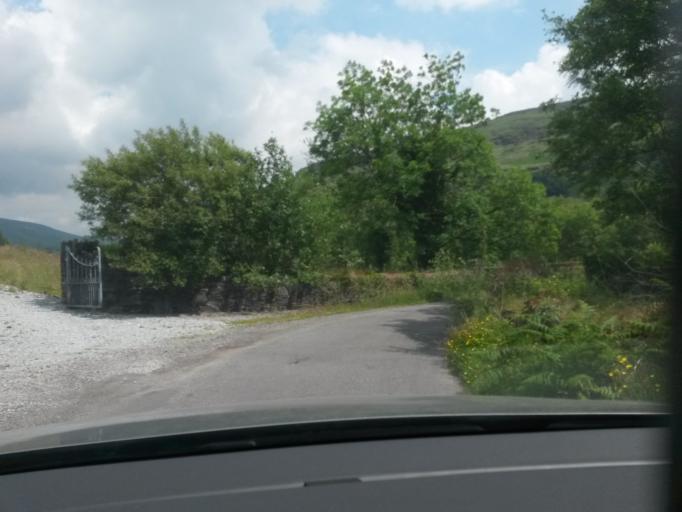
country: IE
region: Munster
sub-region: Ciarrai
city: Kenmare
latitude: 51.8124
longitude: -9.5370
